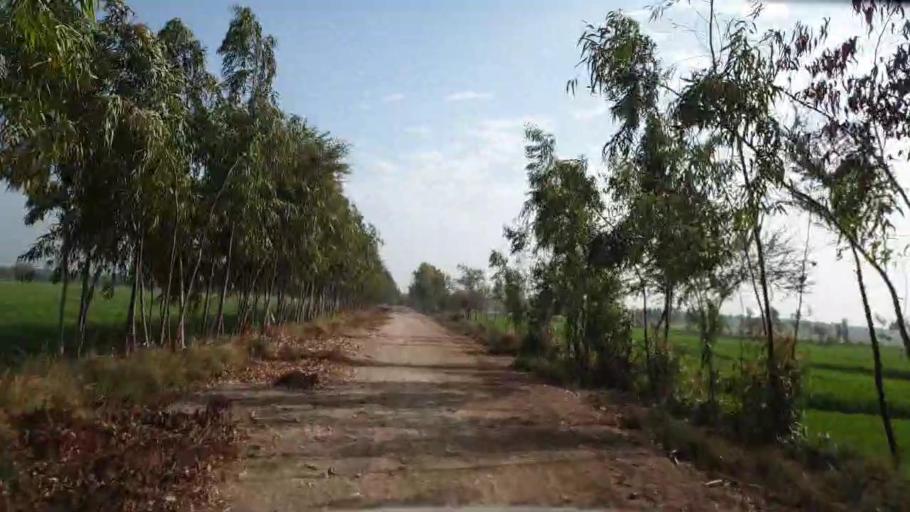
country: PK
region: Sindh
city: Matiari
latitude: 25.6008
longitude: 68.5011
